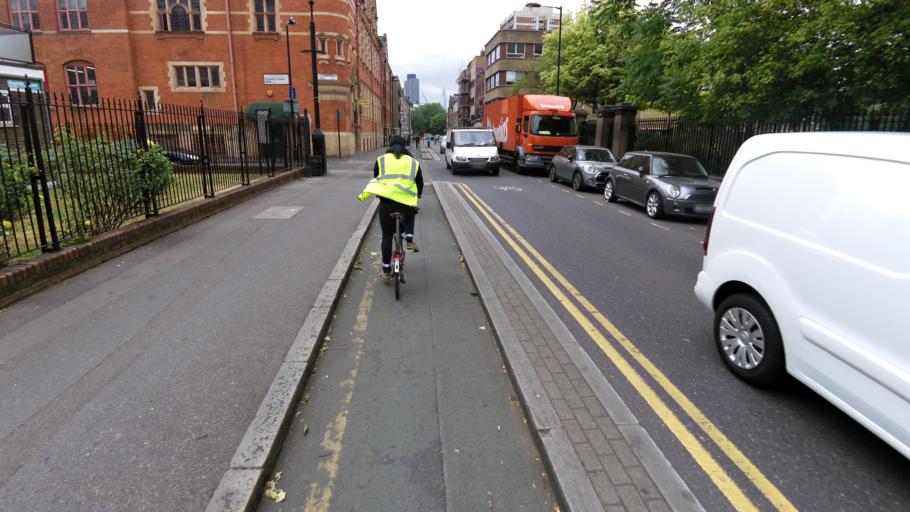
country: GB
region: England
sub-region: Greater London
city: Barbican
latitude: 51.5283
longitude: -0.0835
